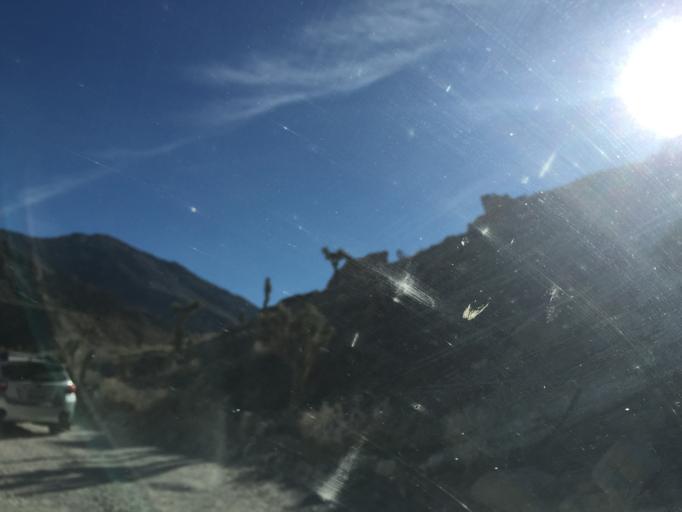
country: US
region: California
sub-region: Inyo County
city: Lone Pine
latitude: 36.8777
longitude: -117.5008
